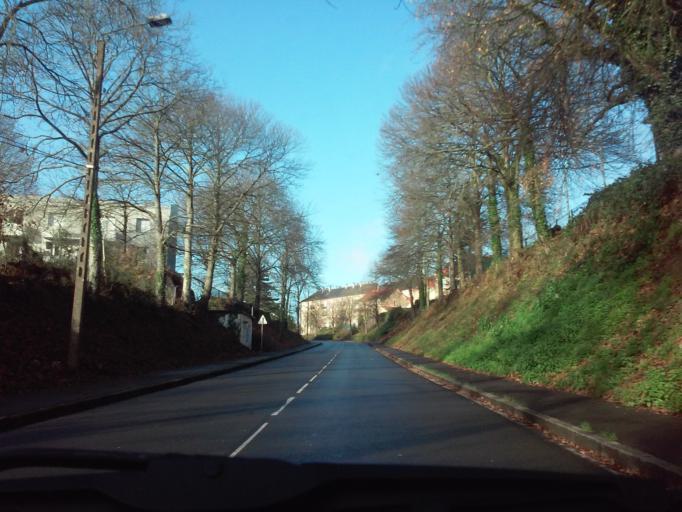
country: FR
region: Brittany
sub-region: Departement d'Ille-et-Vilaine
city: Fougeres
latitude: 48.3422
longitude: -1.1970
